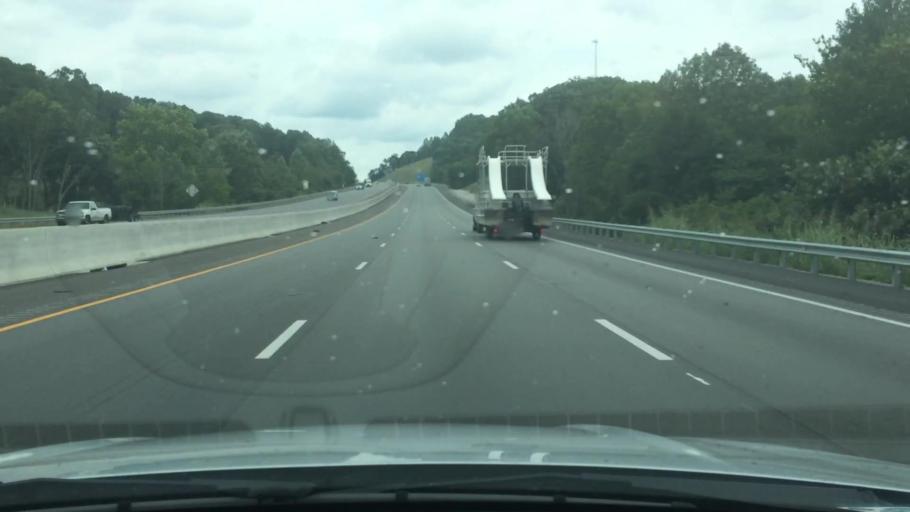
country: US
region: Kentucky
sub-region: Rockcastle County
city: Brodhead
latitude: 37.4446
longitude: -84.3379
